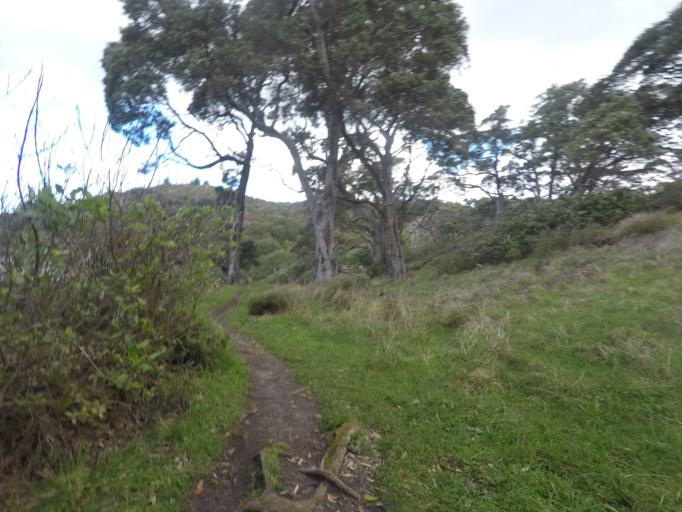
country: NZ
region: Bay of Plenty
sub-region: Western Bay of Plenty District
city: Waihi Beach
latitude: -37.3856
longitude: 175.9390
